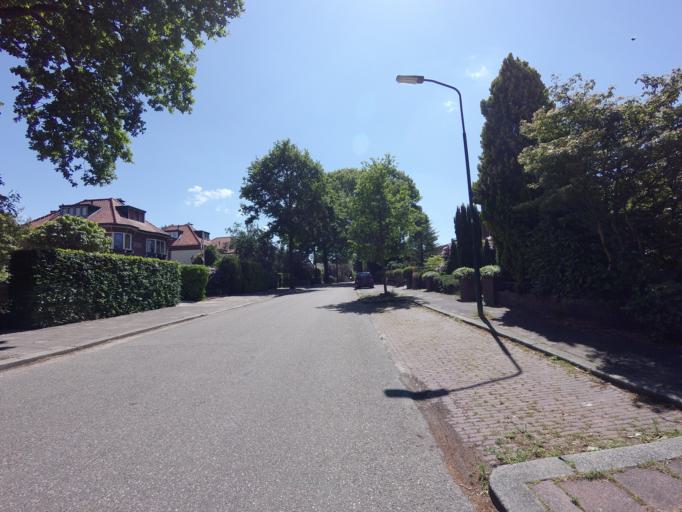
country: NL
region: Utrecht
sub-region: Gemeente Soest
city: Soest
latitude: 52.1829
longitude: 5.2897
